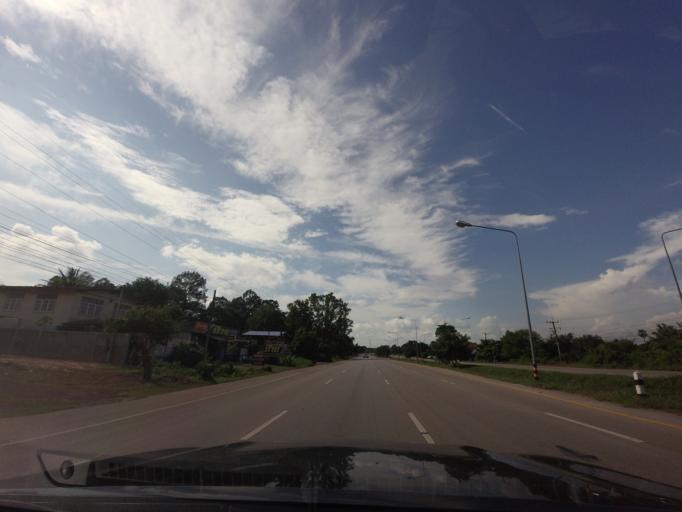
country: TH
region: Nong Khai
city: Sa Khrai
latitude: 17.6769
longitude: 102.7877
